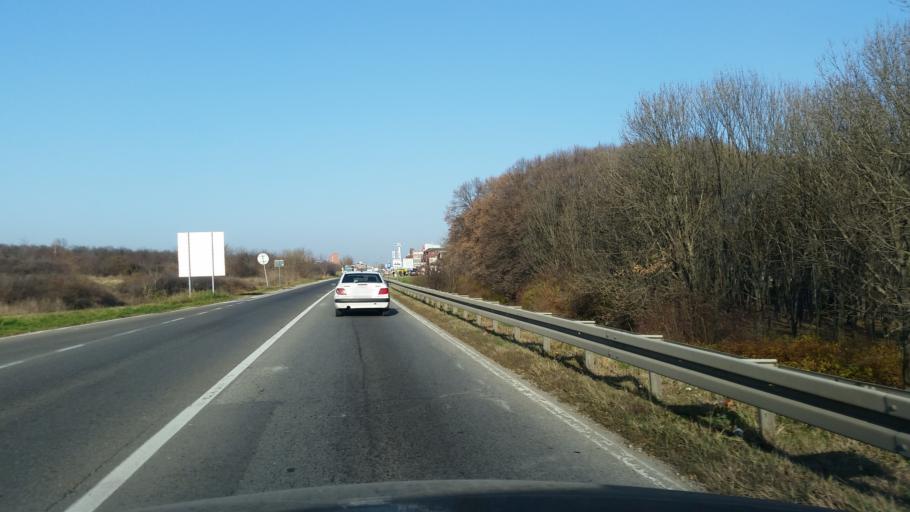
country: RS
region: Central Serbia
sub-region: Belgrade
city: Rakovica
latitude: 44.7201
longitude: 20.4162
